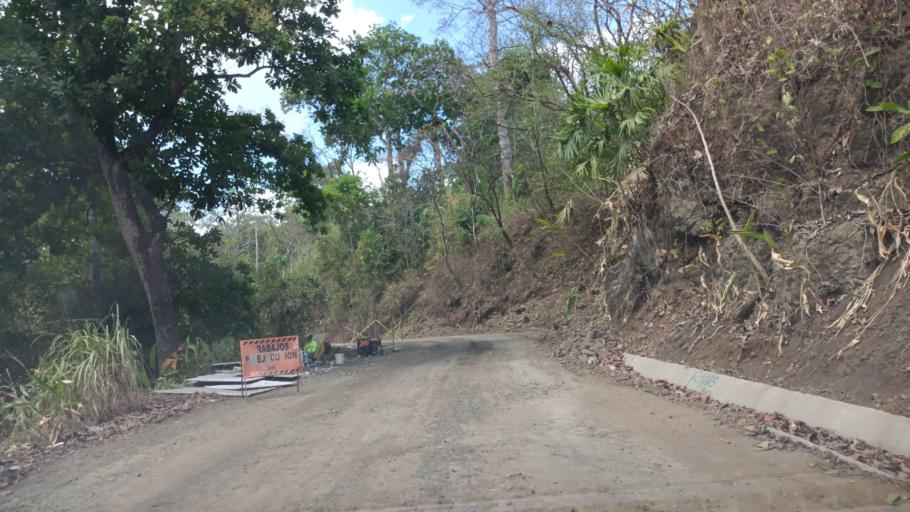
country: PA
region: Panama
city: Las Cumbres
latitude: 9.0754
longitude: -79.5704
